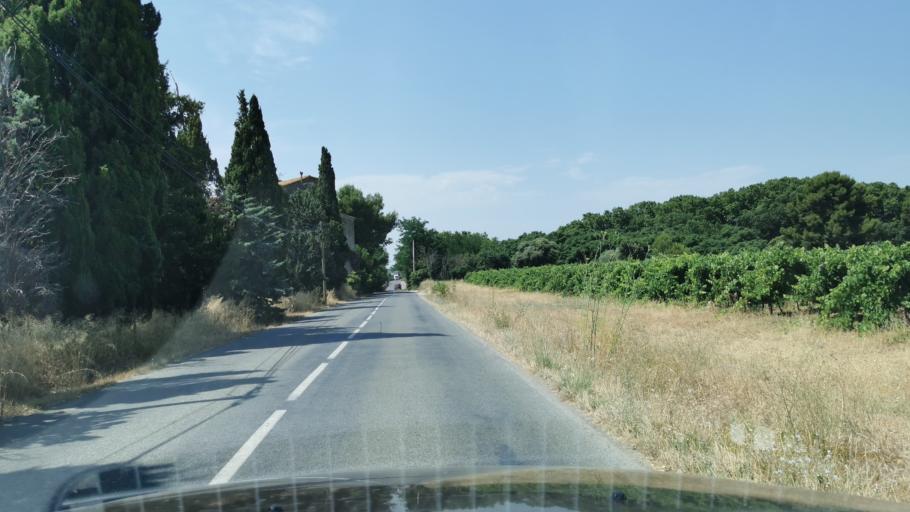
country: FR
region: Languedoc-Roussillon
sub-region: Departement de l'Aude
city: Argeliers
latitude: 43.2858
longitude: 2.9027
